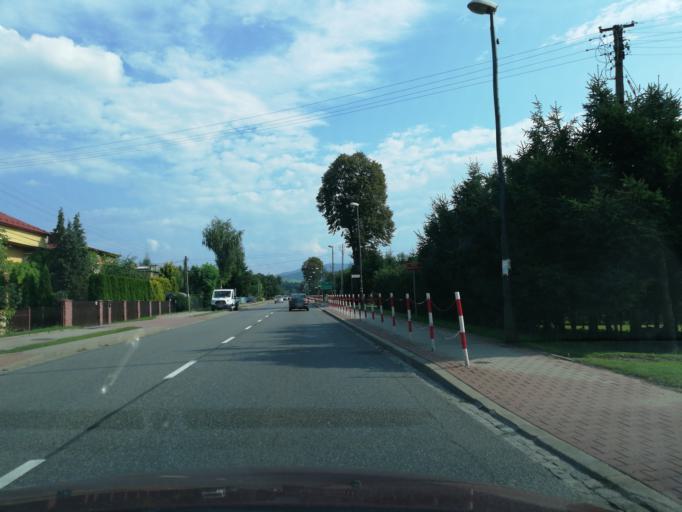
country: PL
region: Lesser Poland Voivodeship
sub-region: Powiat nowosadecki
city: Nawojowa
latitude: 49.5703
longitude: 20.7365
